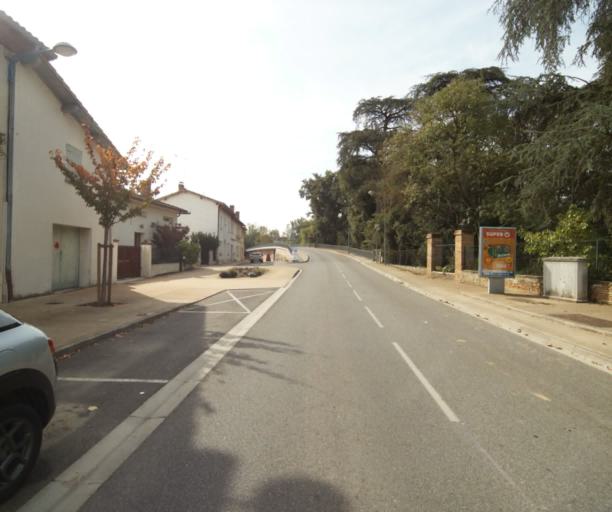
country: FR
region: Midi-Pyrenees
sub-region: Departement du Tarn-et-Garonne
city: Orgueil
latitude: 43.9165
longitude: 1.3973
